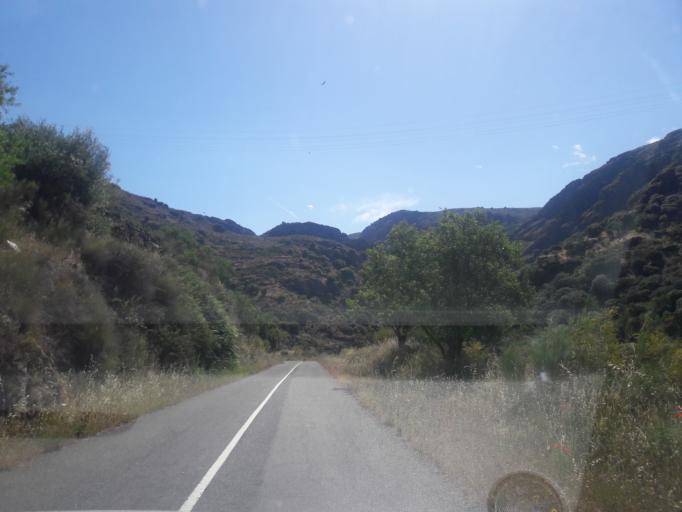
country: ES
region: Castille and Leon
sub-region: Provincia de Salamanca
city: Saucelle
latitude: 41.0299
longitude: -6.7341
